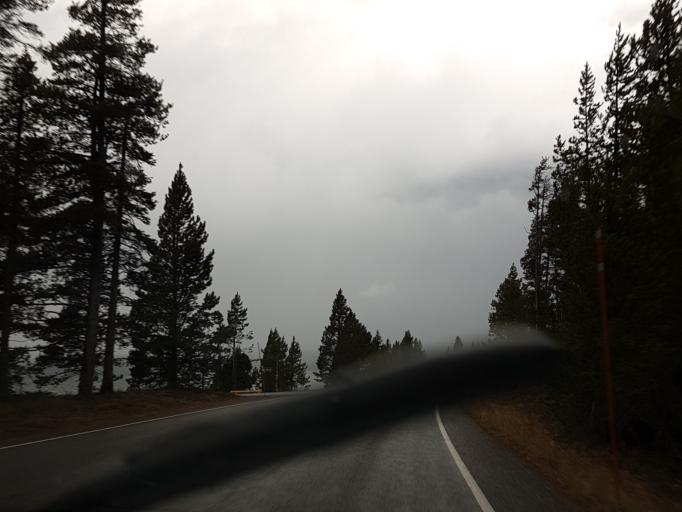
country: US
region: Montana
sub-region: Gallatin County
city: West Yellowstone
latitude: 44.4531
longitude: -110.5039
